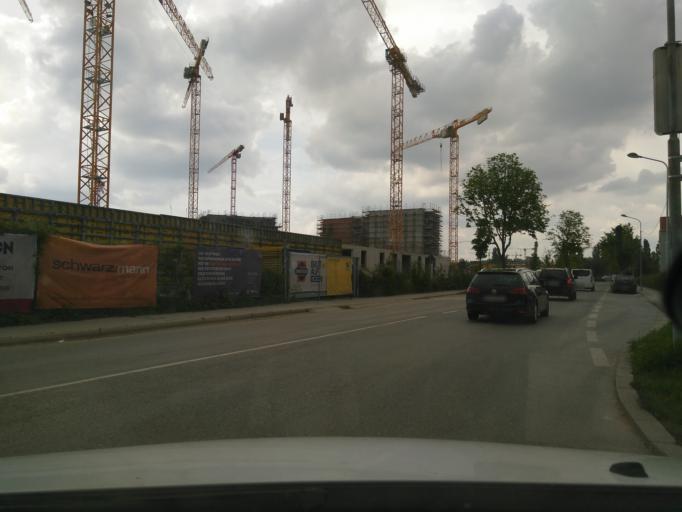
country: AT
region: Lower Austria
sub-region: Politischer Bezirk Modling
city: Perchtoldsdorf
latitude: 48.1492
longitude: 16.2955
